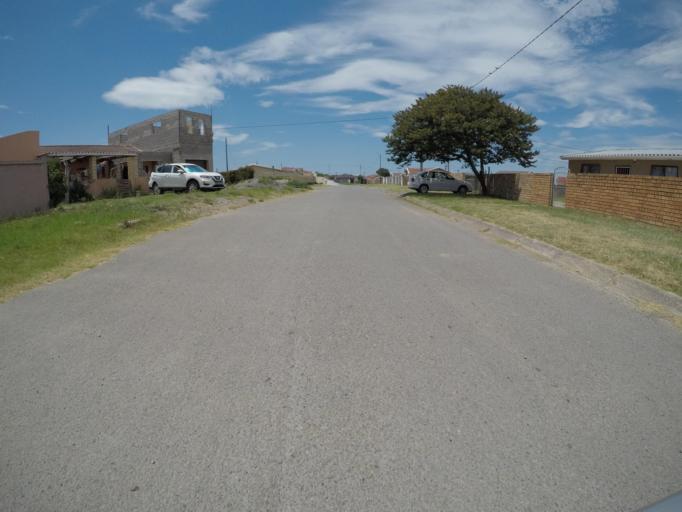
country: ZA
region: Eastern Cape
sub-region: Buffalo City Metropolitan Municipality
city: East London
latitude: -33.0477
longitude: 27.8489
